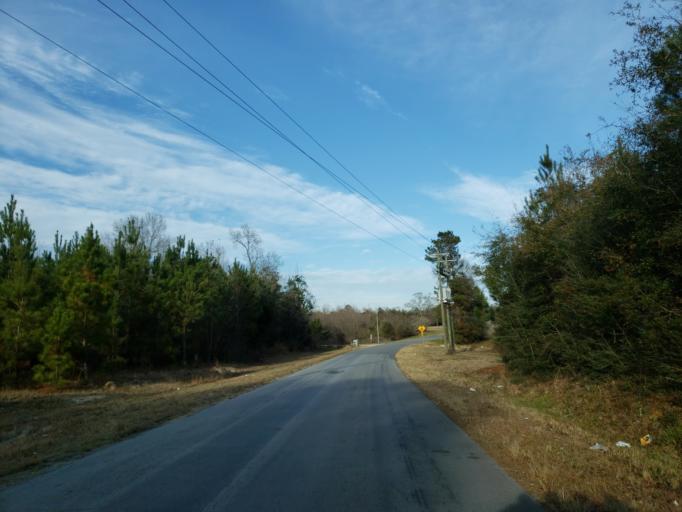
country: US
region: Mississippi
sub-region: Wayne County
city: Belmont
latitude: 31.5081
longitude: -88.5061
